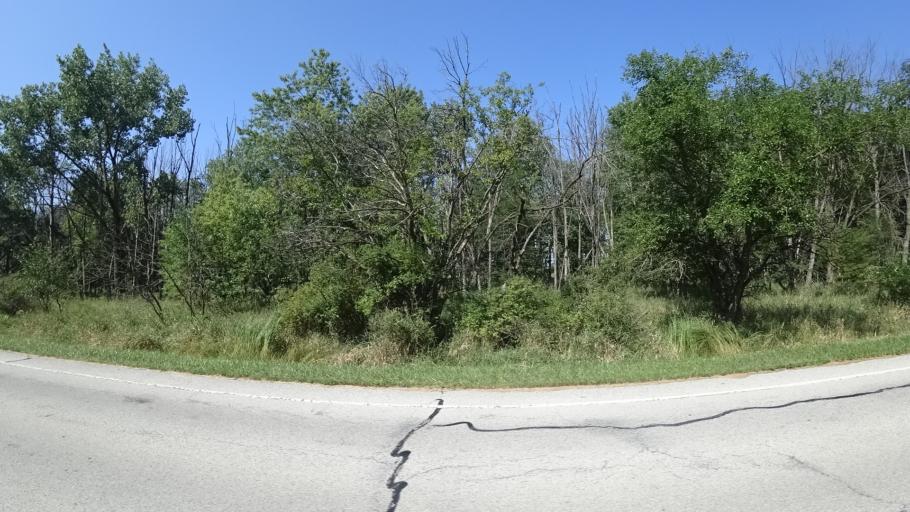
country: US
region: Illinois
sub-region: Cook County
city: Country Club Hills
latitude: 41.5340
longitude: -87.7517
